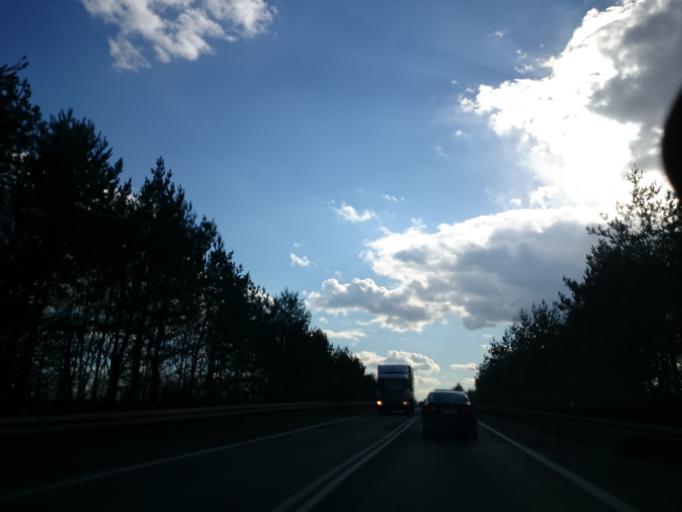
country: PL
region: Opole Voivodeship
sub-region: Powiat opolski
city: Dabrowa
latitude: 50.6631
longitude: 17.6964
